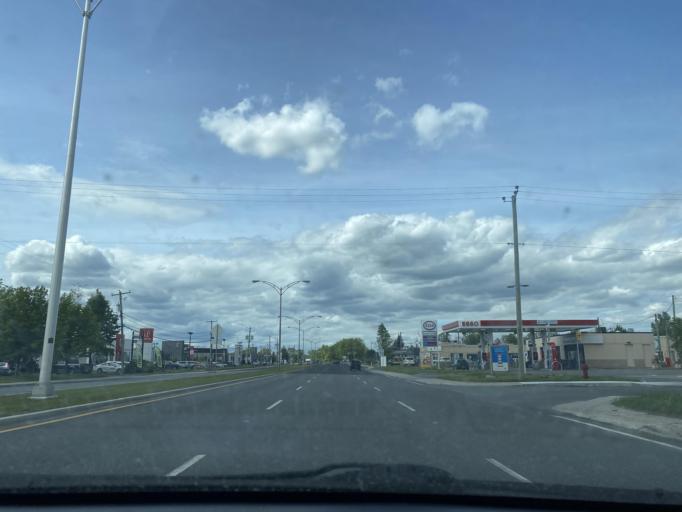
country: CA
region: Quebec
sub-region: Monteregie
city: Carignan
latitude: 45.4540
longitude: -73.3017
